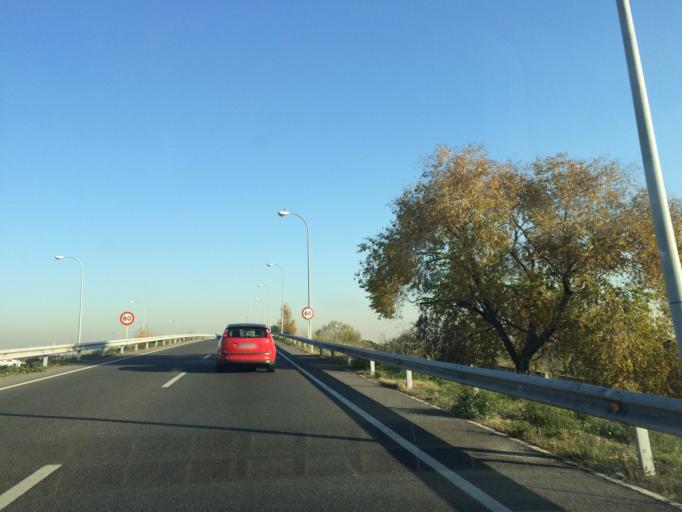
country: ES
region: Madrid
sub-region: Provincia de Madrid
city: Alcorcon
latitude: 40.3617
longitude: -3.7980
